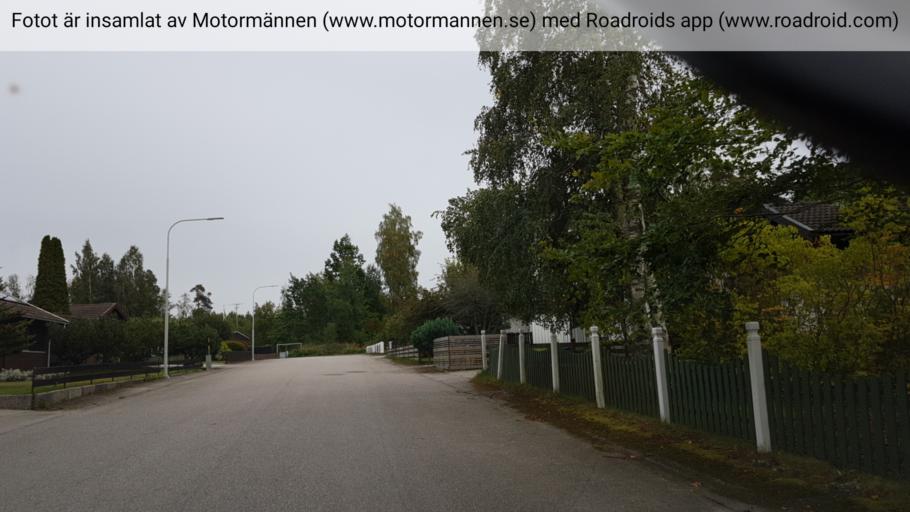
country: SE
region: Vaestra Goetaland
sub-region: Mariestads Kommun
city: Mariestad
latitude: 58.6439
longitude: 13.7032
